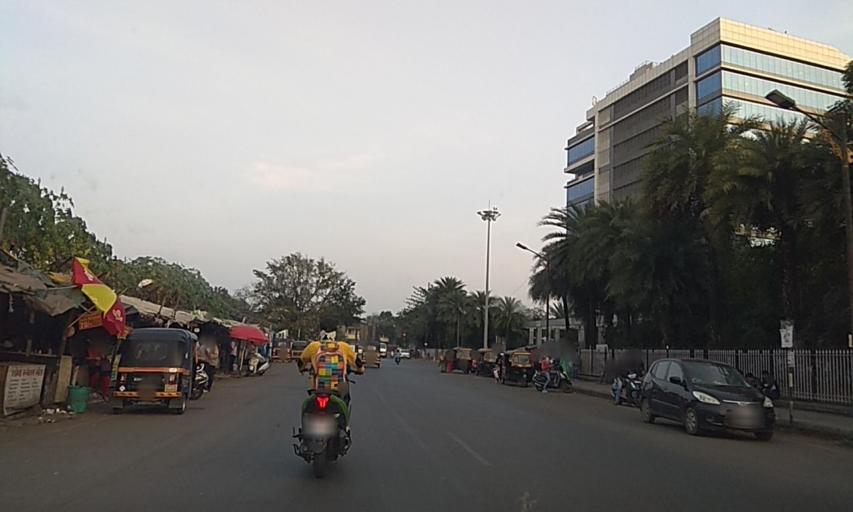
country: IN
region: Maharashtra
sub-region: Pune Division
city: Khadki
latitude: 18.5643
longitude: 73.8836
